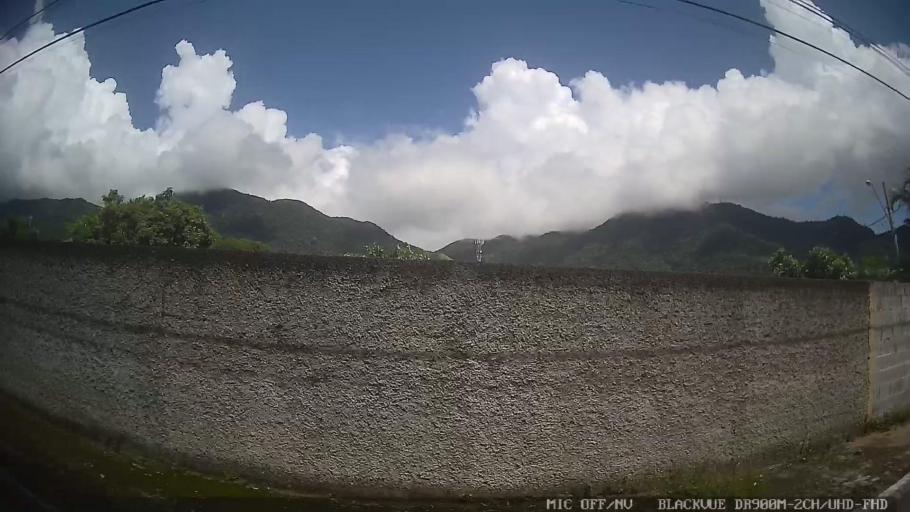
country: BR
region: Sao Paulo
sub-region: Sao Sebastiao
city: Sao Sebastiao
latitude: -23.7635
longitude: -45.4080
